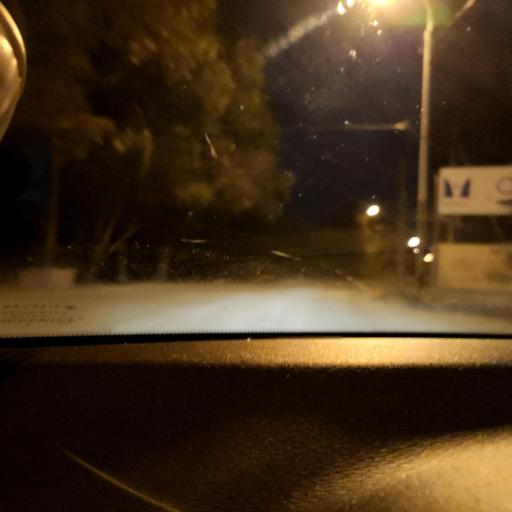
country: RU
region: Samara
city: Samara
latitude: 53.1252
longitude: 50.0969
